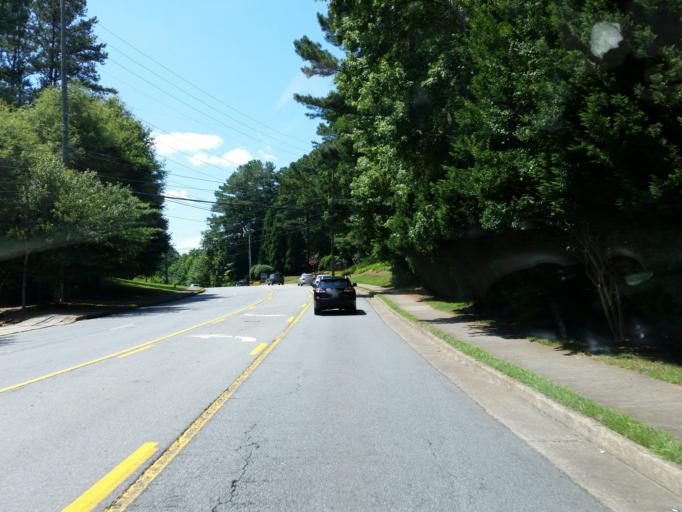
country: US
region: Georgia
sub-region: Cobb County
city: Smyrna
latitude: 33.9295
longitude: -84.4736
